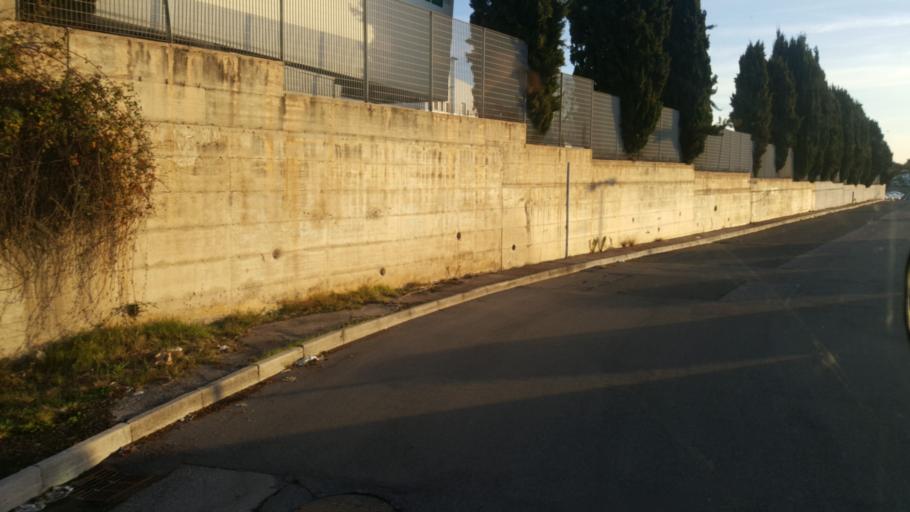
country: IT
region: Latium
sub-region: Citta metropolitana di Roma Capitale
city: Formello
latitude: 42.0533
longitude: 12.3995
